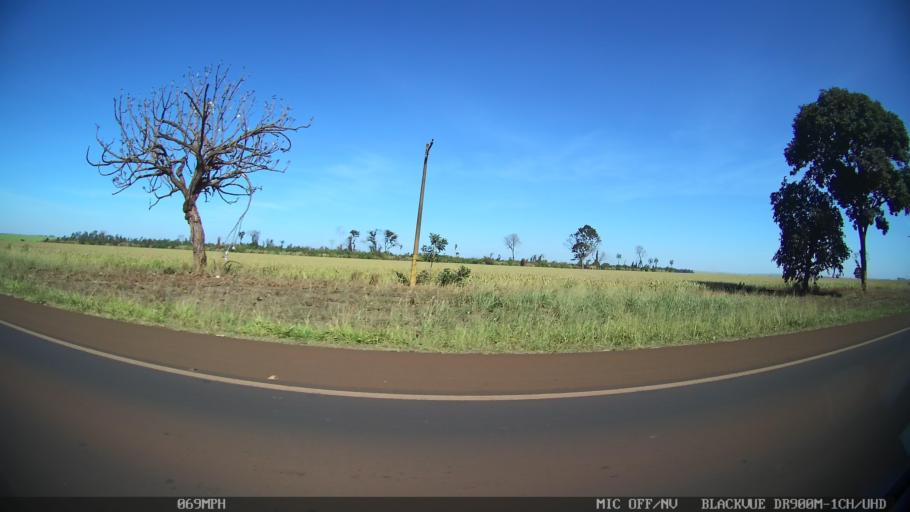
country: BR
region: Sao Paulo
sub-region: Guaira
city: Guaira
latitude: -20.4451
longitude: -48.3953
